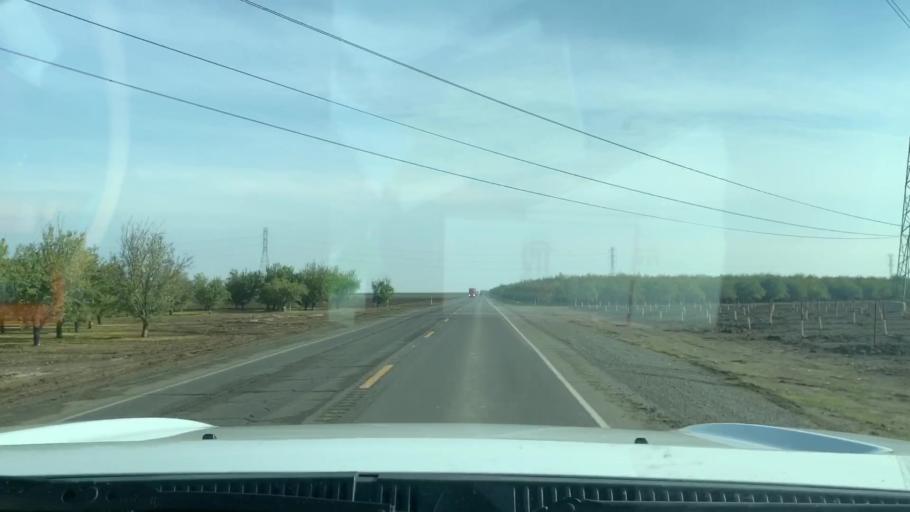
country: US
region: California
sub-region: Fresno County
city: Huron
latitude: 36.2547
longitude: -120.2213
